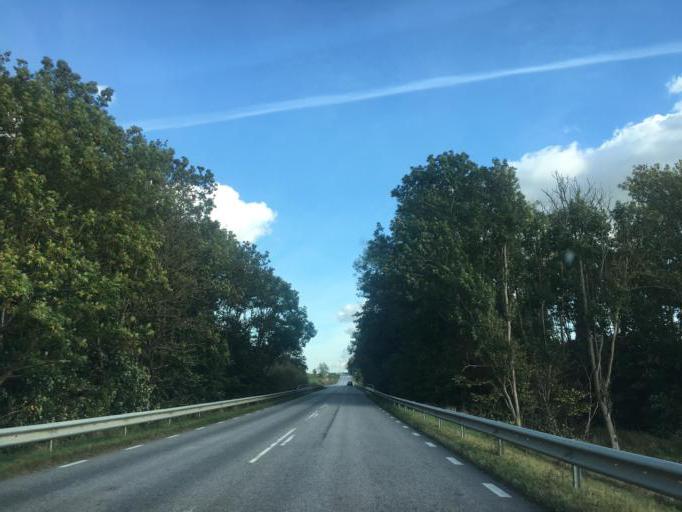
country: SE
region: Skane
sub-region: Eslovs Kommun
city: Eslov
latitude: 55.7888
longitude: 13.2422
